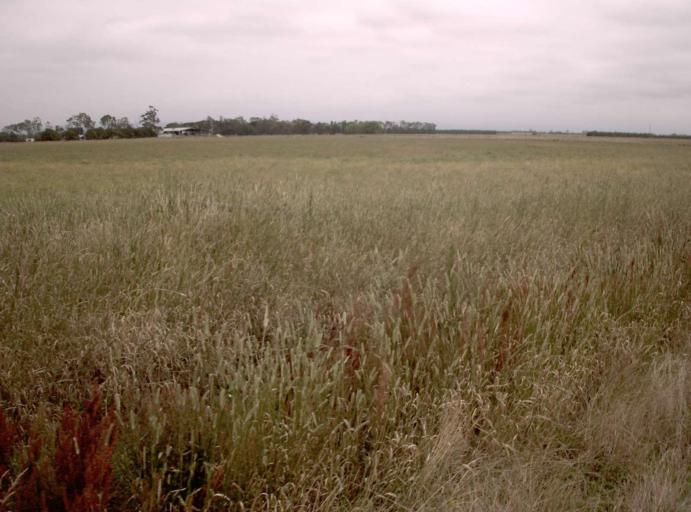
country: AU
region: Victoria
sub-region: Wellington
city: Heyfield
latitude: -38.0976
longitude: 146.7731
